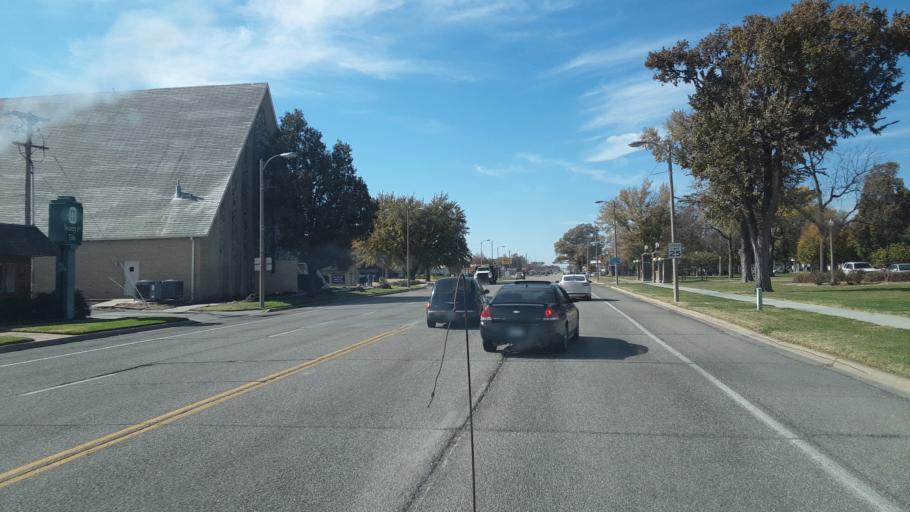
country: US
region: Kansas
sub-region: McPherson County
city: McPherson
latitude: 38.3694
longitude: -97.6685
